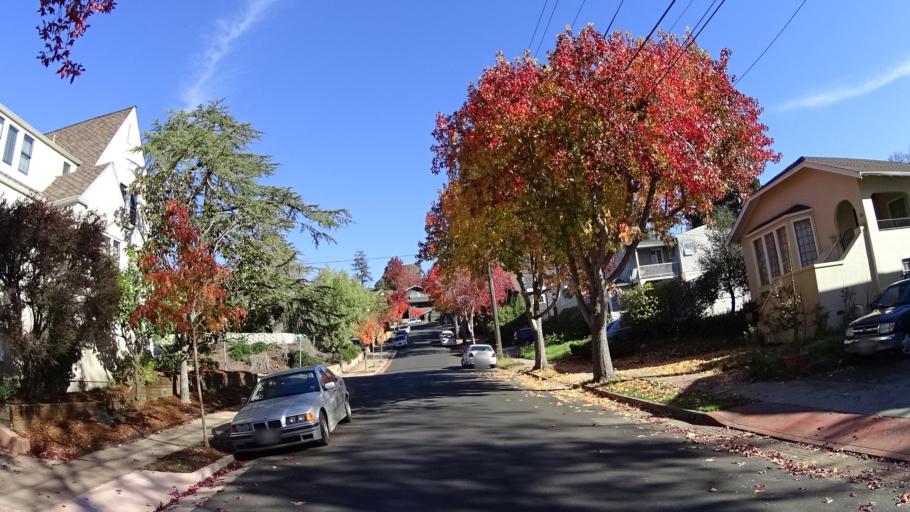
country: US
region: California
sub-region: Alameda County
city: Piedmont
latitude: 37.8250
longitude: -122.2413
